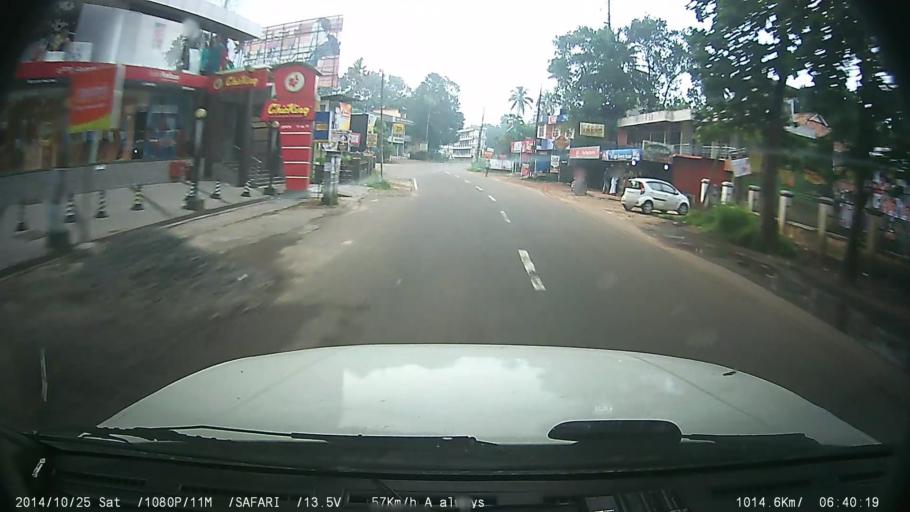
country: IN
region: Kerala
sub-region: Ernakulam
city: Muvattupuzha
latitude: 9.9758
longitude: 76.5798
